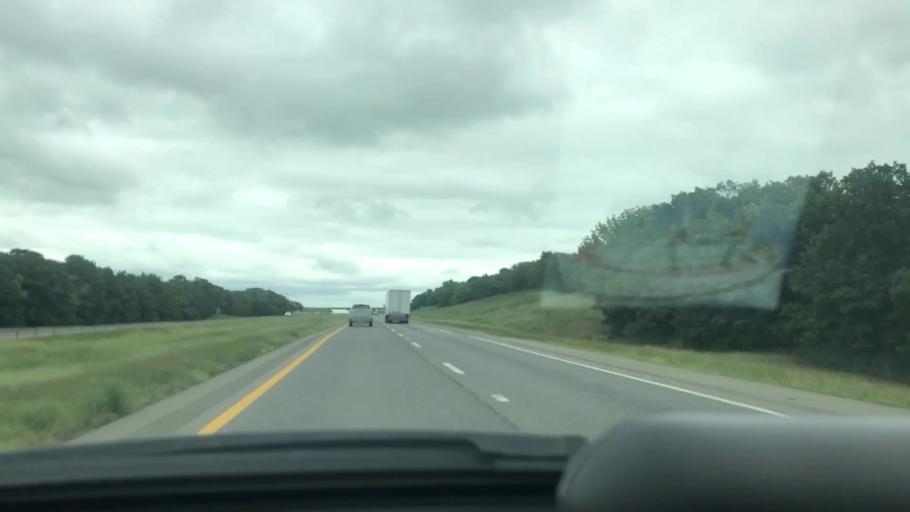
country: US
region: Oklahoma
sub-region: McIntosh County
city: Checotah
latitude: 35.3970
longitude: -95.5635
